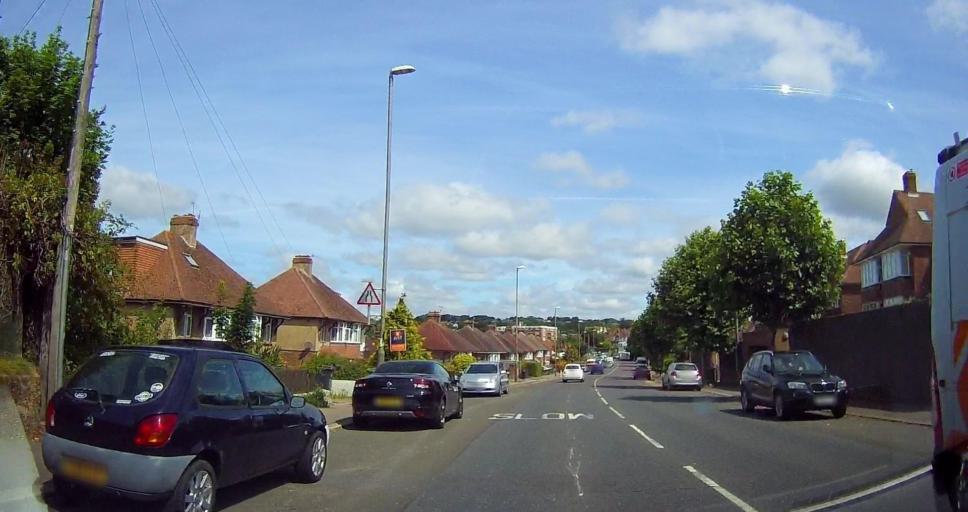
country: GB
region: England
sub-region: East Sussex
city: Saint Leonards-on-Sea
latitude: 50.8728
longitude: 0.5583
